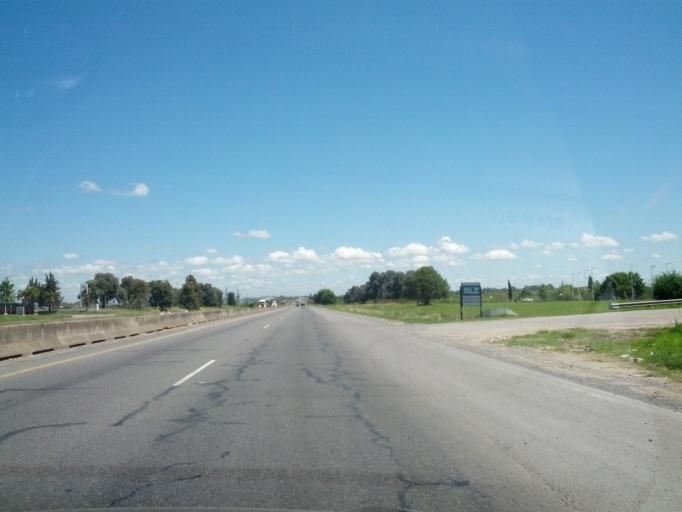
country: AR
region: Buenos Aires
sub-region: Partido de Zarate
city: Zarate
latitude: -34.1233
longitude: -59.0214
